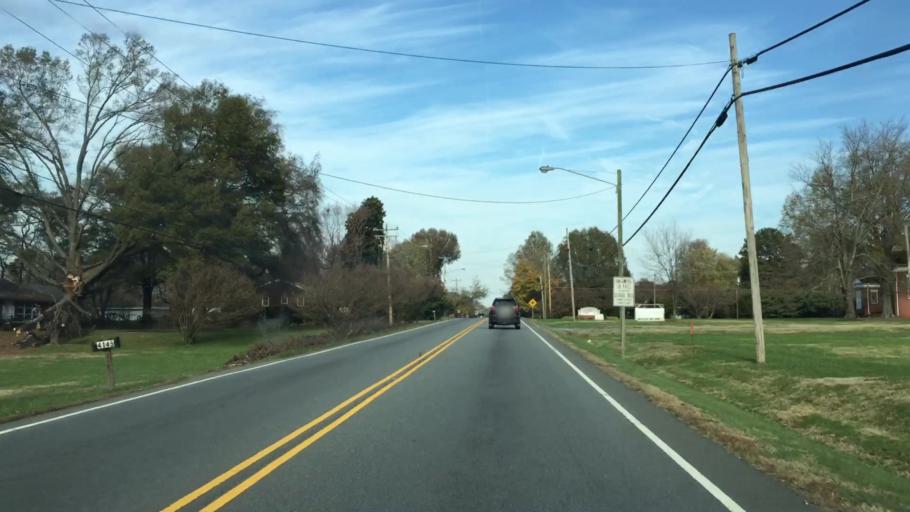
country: US
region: North Carolina
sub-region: Forsyth County
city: Walkertown
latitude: 36.1206
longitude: -80.1820
